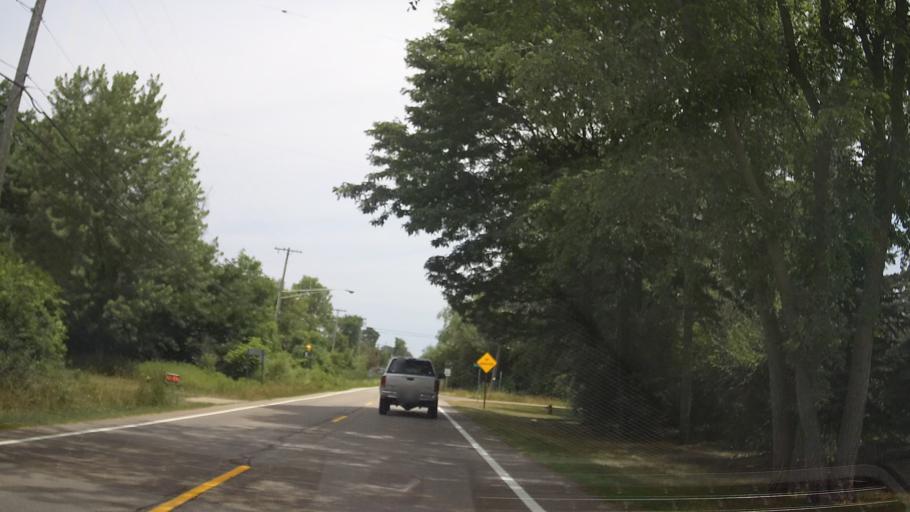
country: US
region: Michigan
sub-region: Oakland County
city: Troy
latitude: 42.6072
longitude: -83.1210
